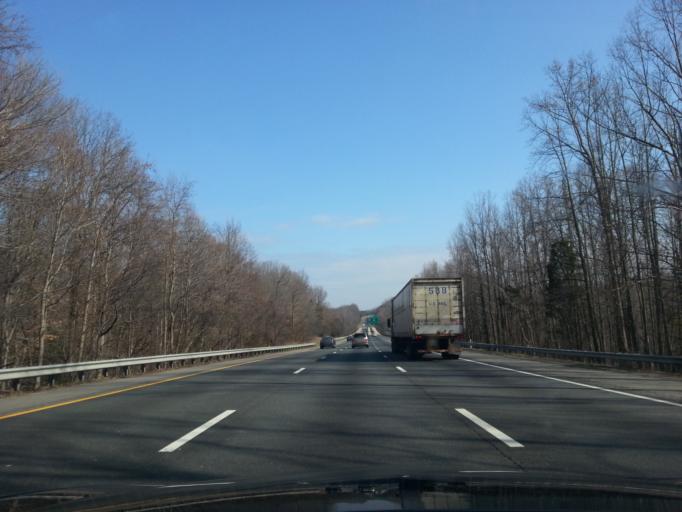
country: US
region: Virginia
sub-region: Stafford County
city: Falmouth
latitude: 38.3221
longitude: -77.5030
